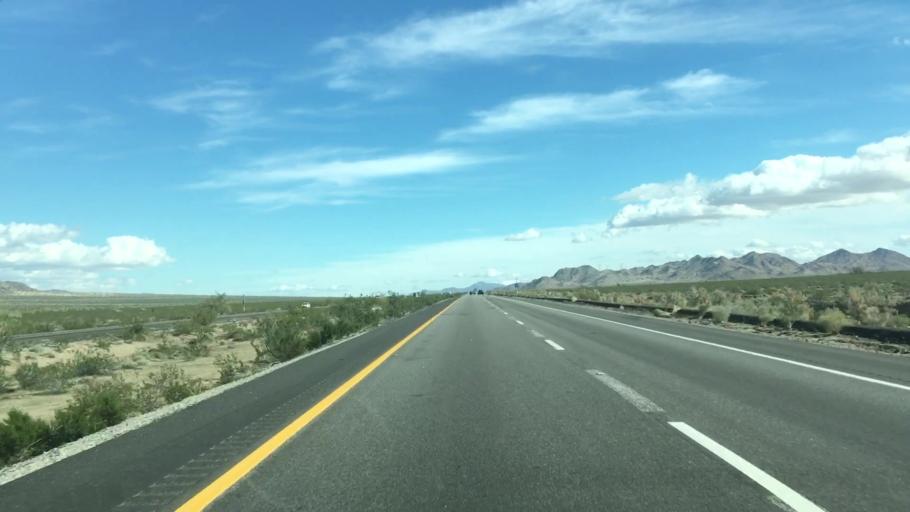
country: US
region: California
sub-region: Riverside County
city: Mecca
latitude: 33.6600
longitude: -115.7789
